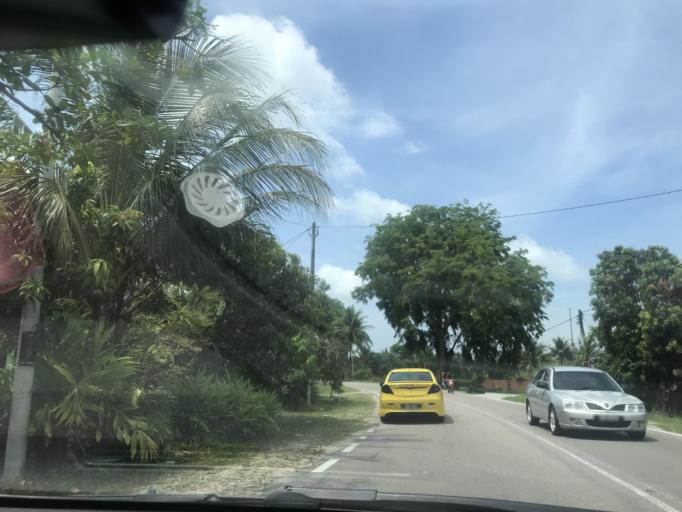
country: MY
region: Kelantan
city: Tumpat
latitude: 6.2027
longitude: 102.1499
